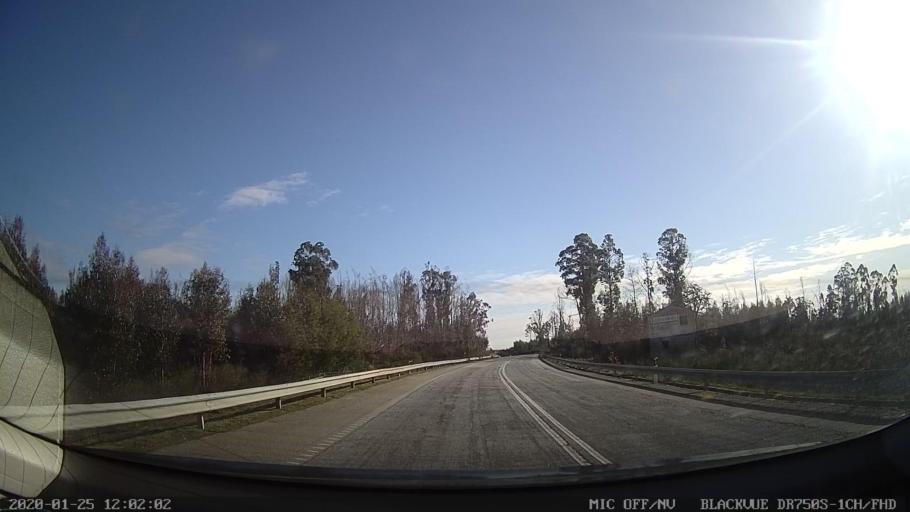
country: PT
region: Viseu
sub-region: Viseu
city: Abraveses
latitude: 40.6548
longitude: -8.0262
